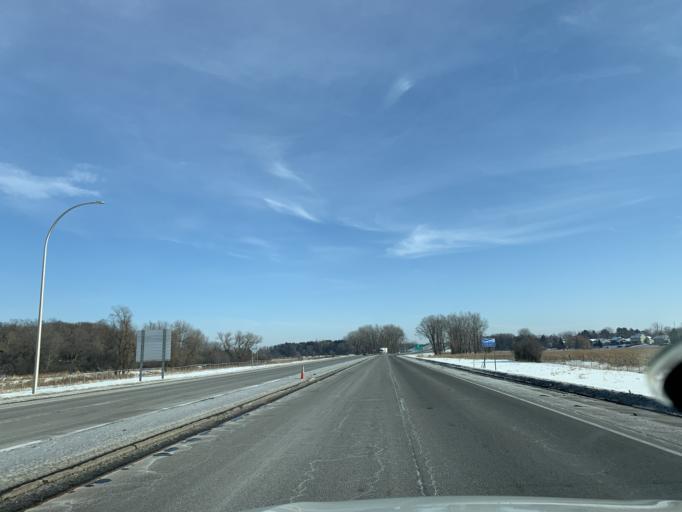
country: US
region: Minnesota
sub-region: Washington County
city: Forest Lake
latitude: 45.2897
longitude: -92.9978
